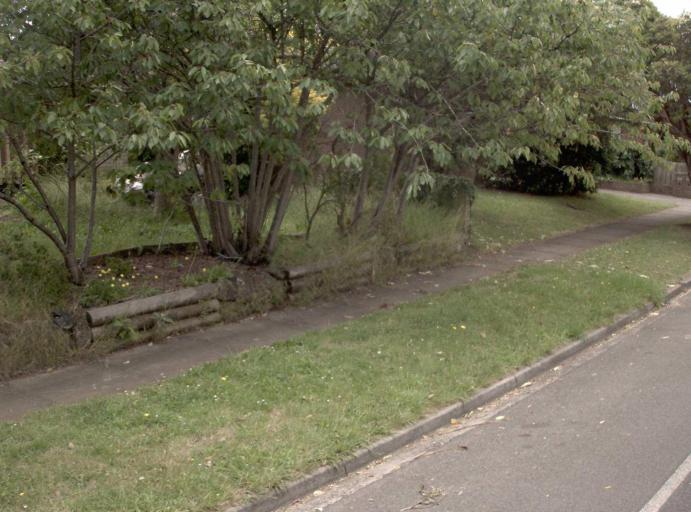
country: AU
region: Victoria
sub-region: Baw Baw
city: Warragul
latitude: -38.1435
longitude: 145.9387
